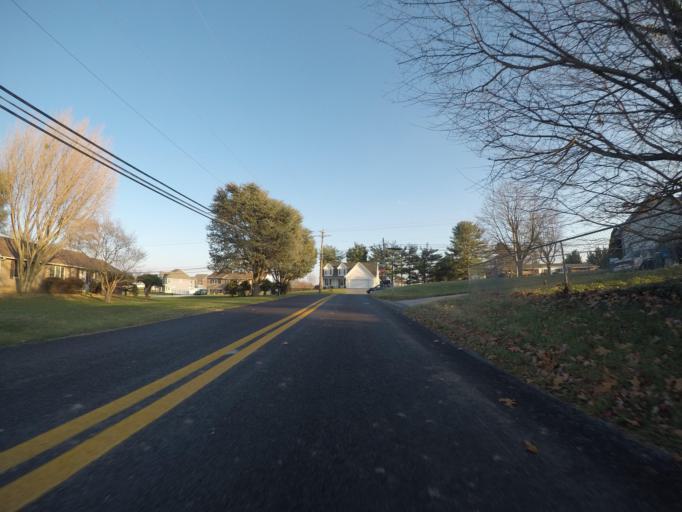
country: US
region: Maryland
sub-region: Carroll County
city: Hampstead
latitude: 39.5873
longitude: -76.8650
